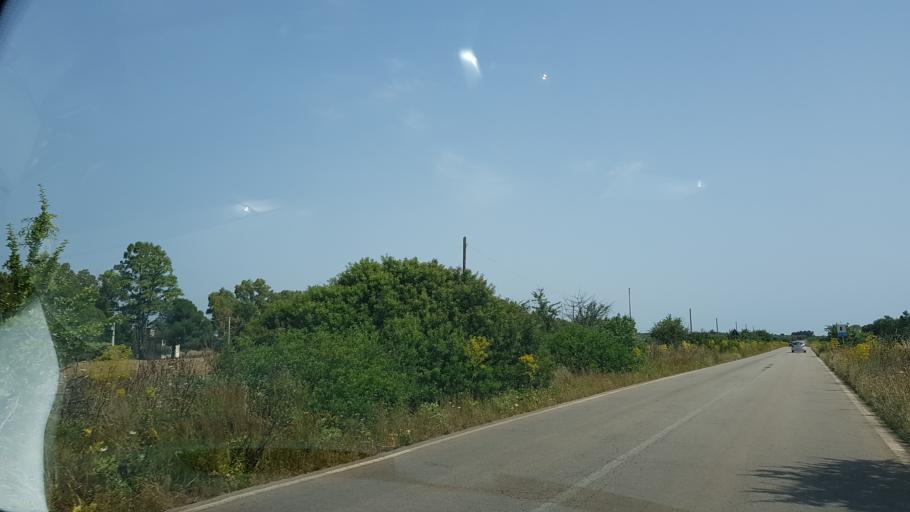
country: IT
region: Apulia
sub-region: Provincia di Brindisi
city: San Pancrazio Salentino
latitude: 40.3372
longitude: 17.8499
